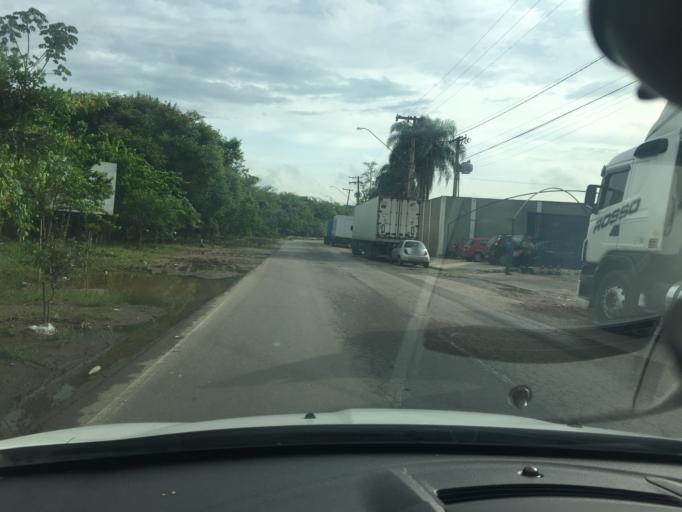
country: BR
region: Sao Paulo
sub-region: Campo Limpo Paulista
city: Campo Limpo Paulista
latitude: -23.2049
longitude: -46.8031
